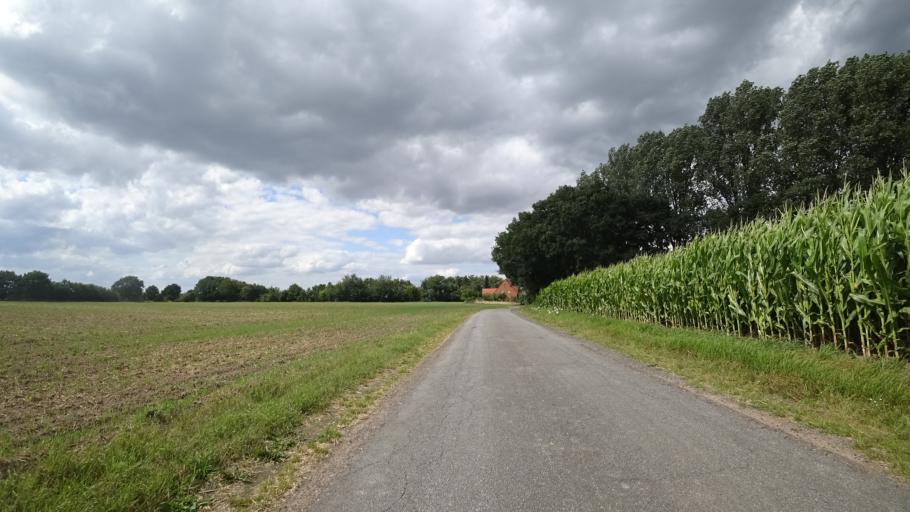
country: DE
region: Lower Saxony
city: Raddestorf
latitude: 52.4298
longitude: 9.0303
